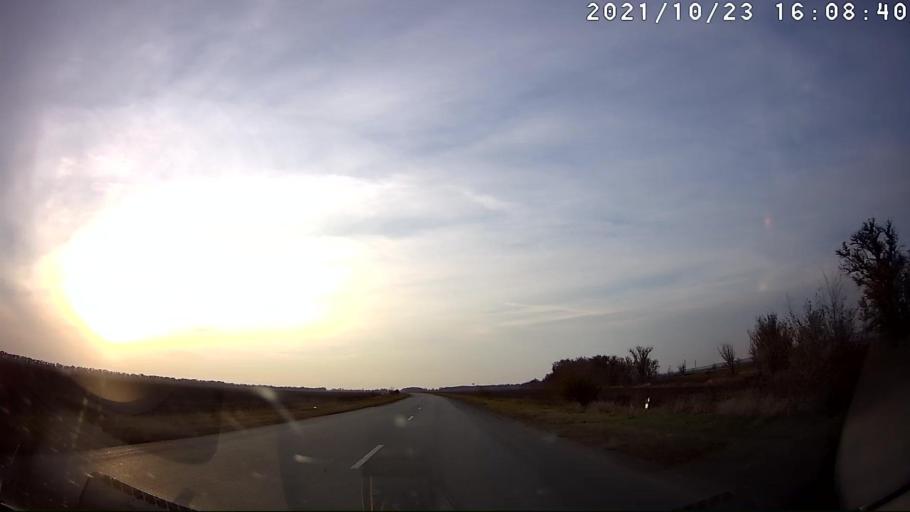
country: RU
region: Volgograd
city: Kotel'nikovo
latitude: 47.9422
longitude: 43.7122
